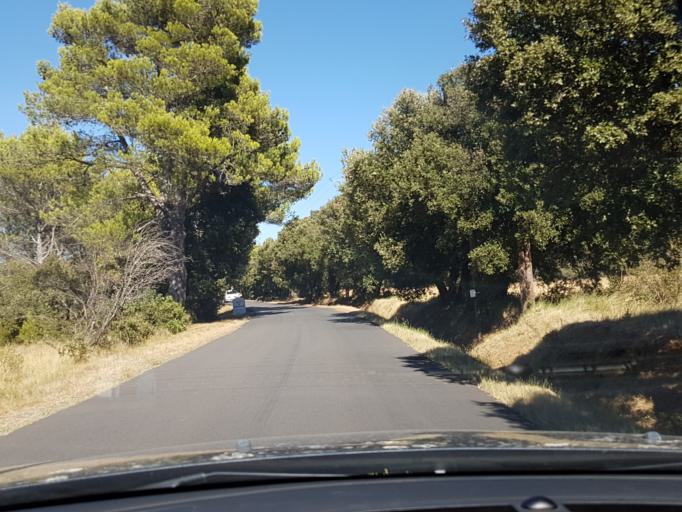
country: FR
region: Provence-Alpes-Cote d'Azur
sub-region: Departement des Bouches-du-Rhone
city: Orgon
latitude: 43.7769
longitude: 5.0046
